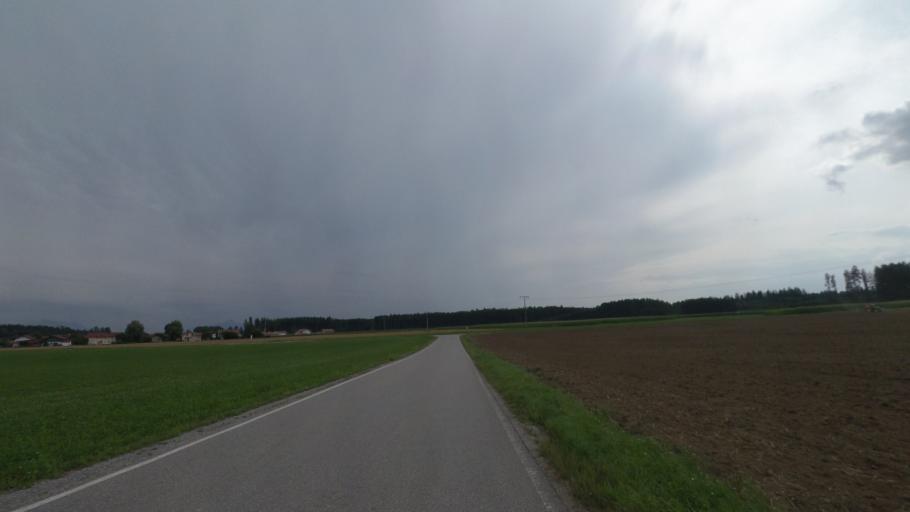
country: DE
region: Bavaria
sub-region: Upper Bavaria
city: Pittenhart
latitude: 47.9801
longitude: 12.3835
